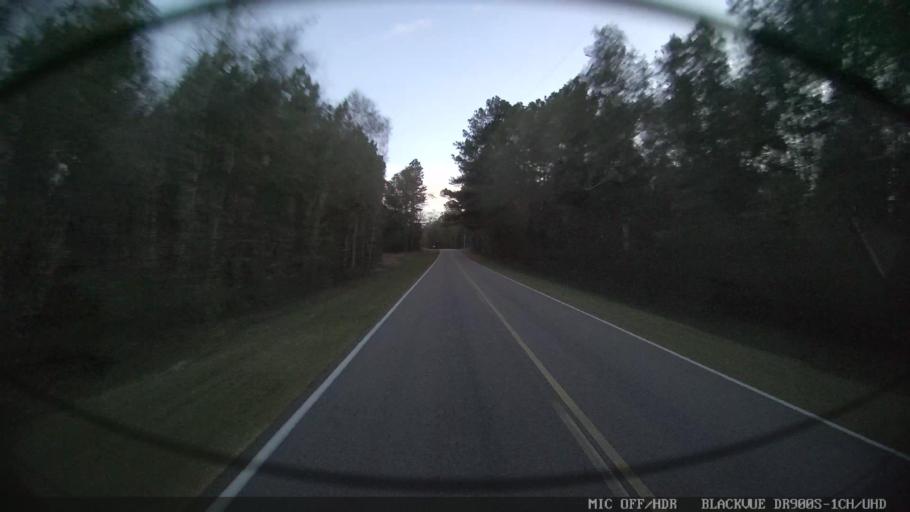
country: US
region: Mississippi
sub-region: Perry County
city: New Augusta
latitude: 31.1089
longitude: -89.1945
